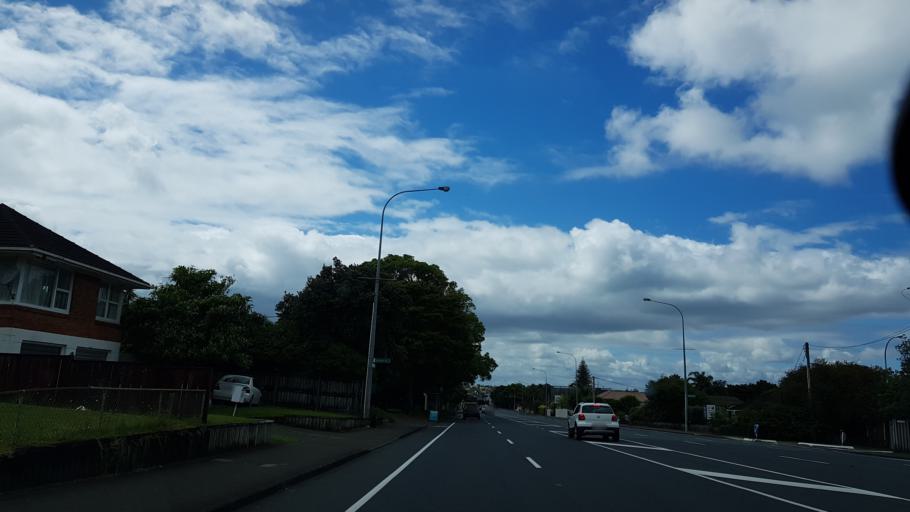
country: NZ
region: Auckland
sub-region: Auckland
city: North Shore
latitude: -36.7874
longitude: 174.7588
